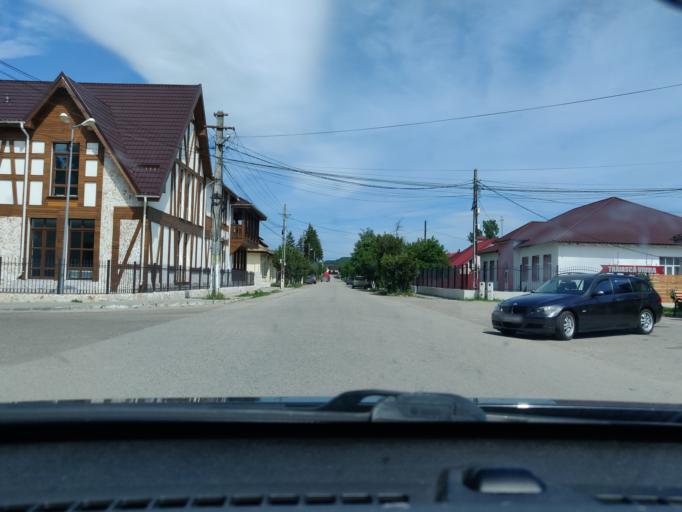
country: RO
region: Vrancea
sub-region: Comuna Vidra
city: Vidra
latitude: 45.9110
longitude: 26.9058
